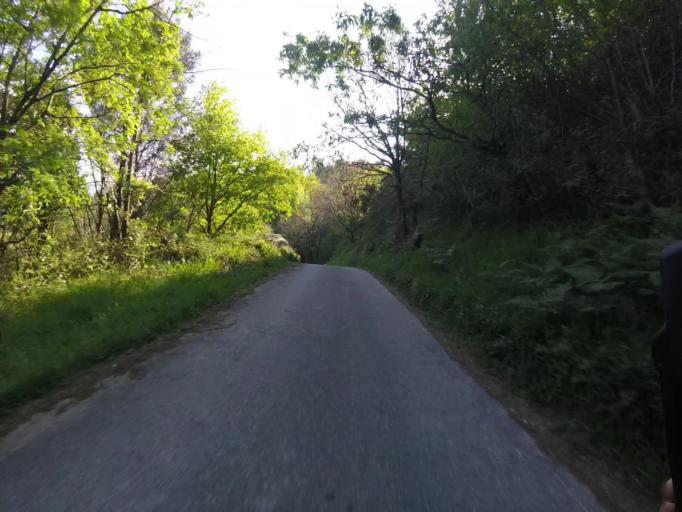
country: ES
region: Basque Country
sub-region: Provincia de Guipuzcoa
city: Pasaia
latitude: 43.3303
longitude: -1.9138
